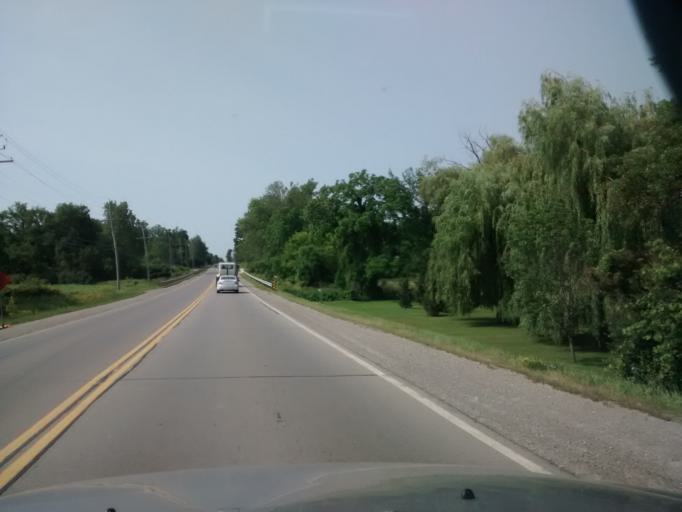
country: CA
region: Ontario
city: Hamilton
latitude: 43.1455
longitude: -79.7940
